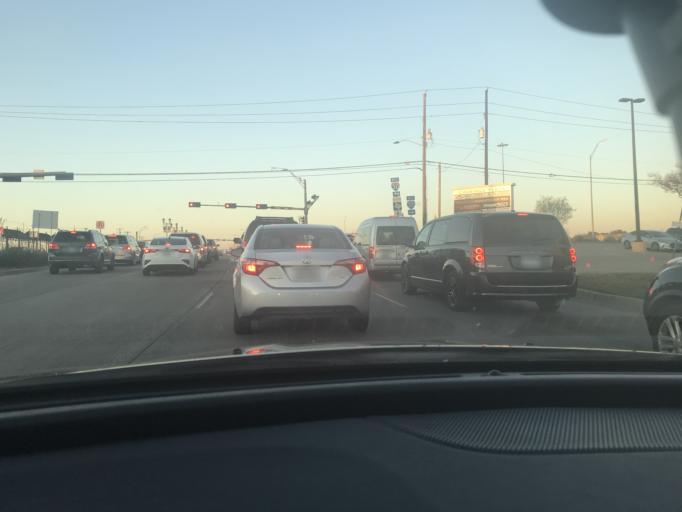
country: US
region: Texas
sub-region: Tarrant County
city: Arlington
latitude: 32.7586
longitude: -97.0971
